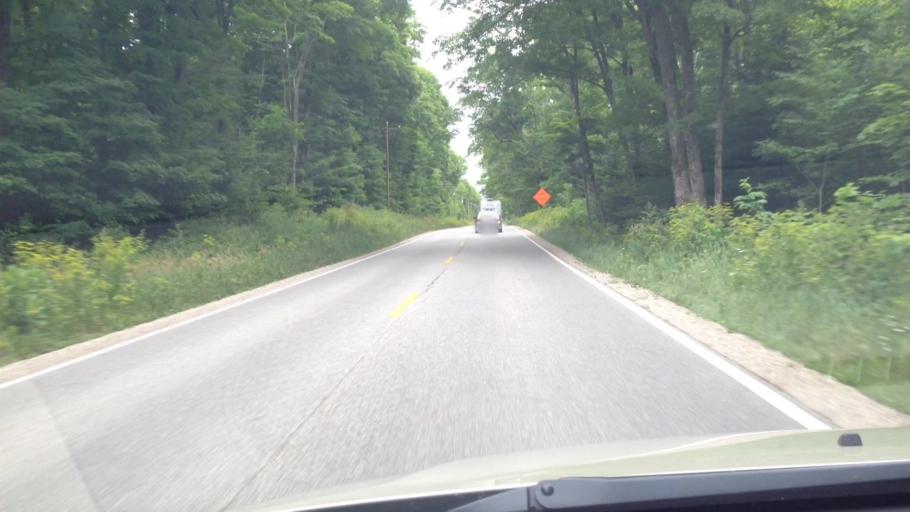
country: US
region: Michigan
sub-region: Mackinac County
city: Saint Ignace
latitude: 46.0569
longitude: -85.1256
